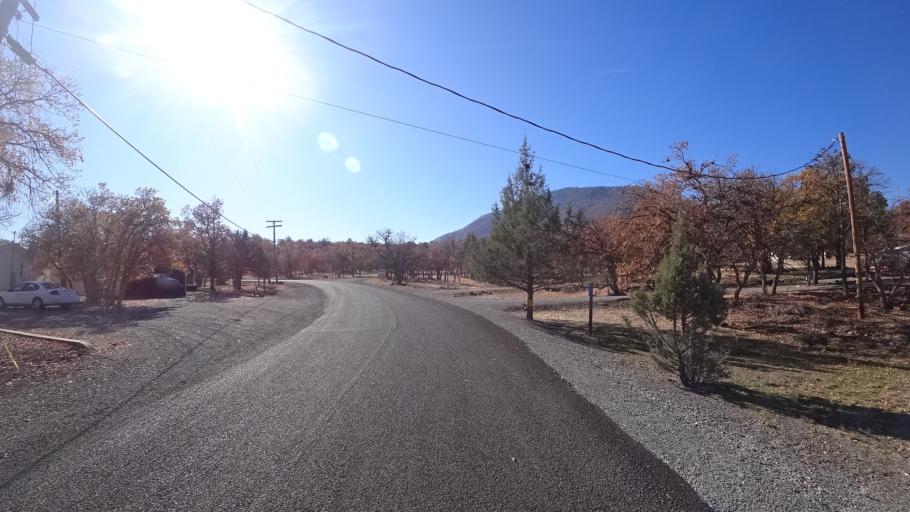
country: US
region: California
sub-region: Siskiyou County
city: Montague
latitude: 41.8815
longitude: -122.4846
